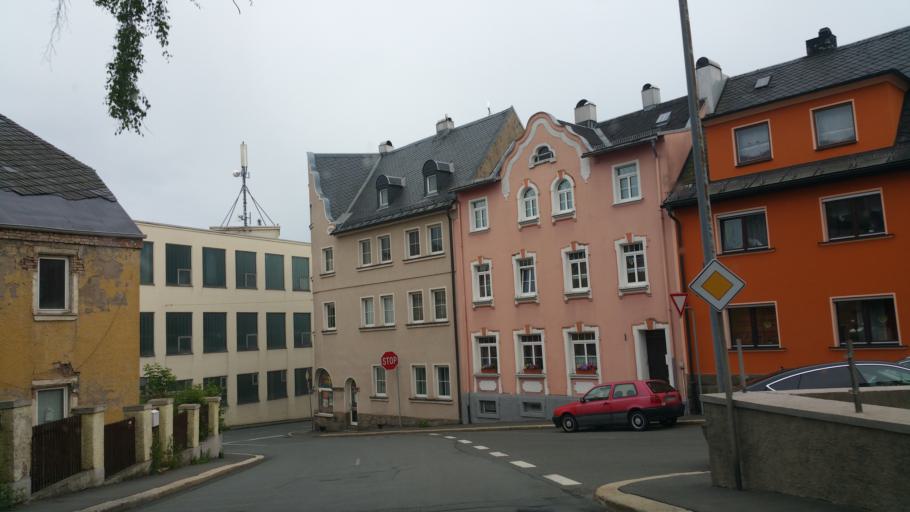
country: DE
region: Bavaria
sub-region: Upper Franconia
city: Helmbrechts
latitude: 50.2408
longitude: 11.7183
